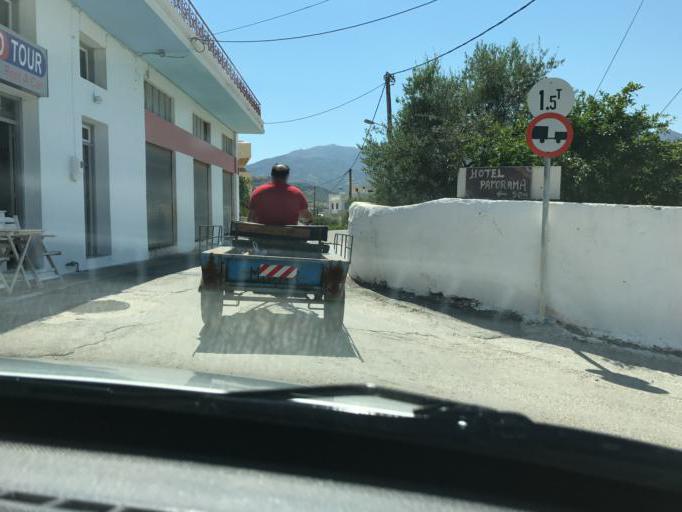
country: GR
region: South Aegean
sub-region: Nomos Dodekanisou
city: Karpathos
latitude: 35.5076
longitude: 27.2061
